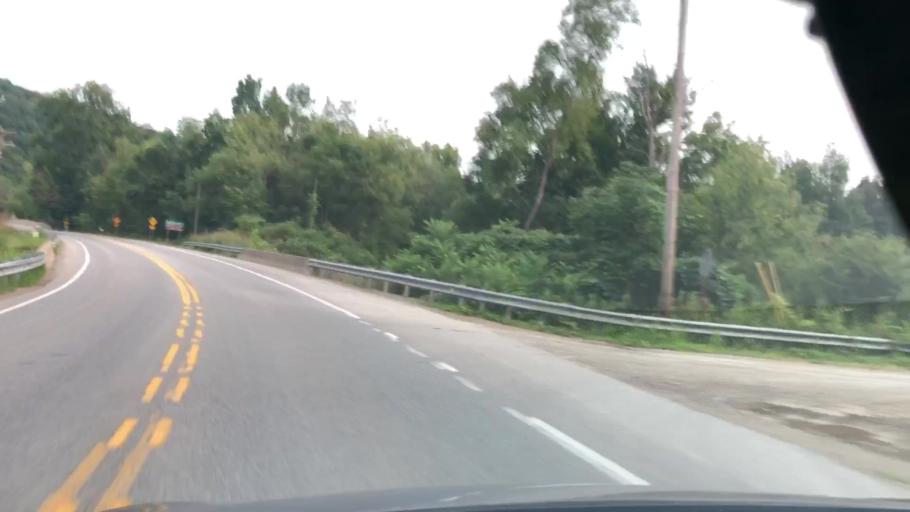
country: US
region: Pennsylvania
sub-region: Venango County
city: Hasson Heights
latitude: 41.4834
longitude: -79.6978
